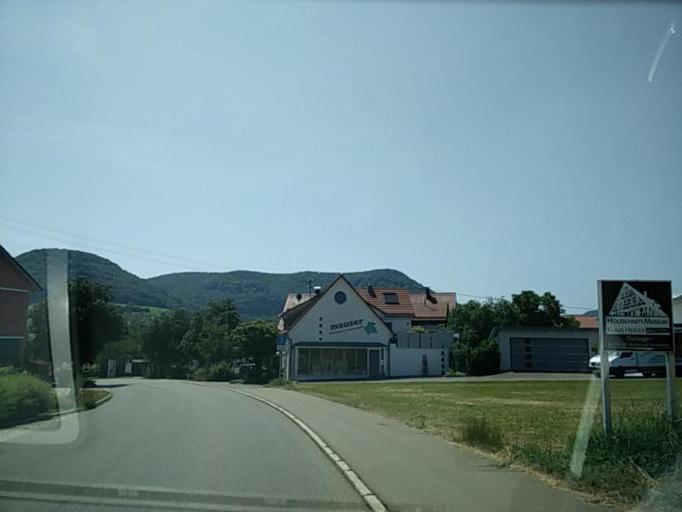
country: DE
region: Baden-Wuerttemberg
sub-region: Tuebingen Region
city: Gomaringen
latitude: 48.4181
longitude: 9.1106
